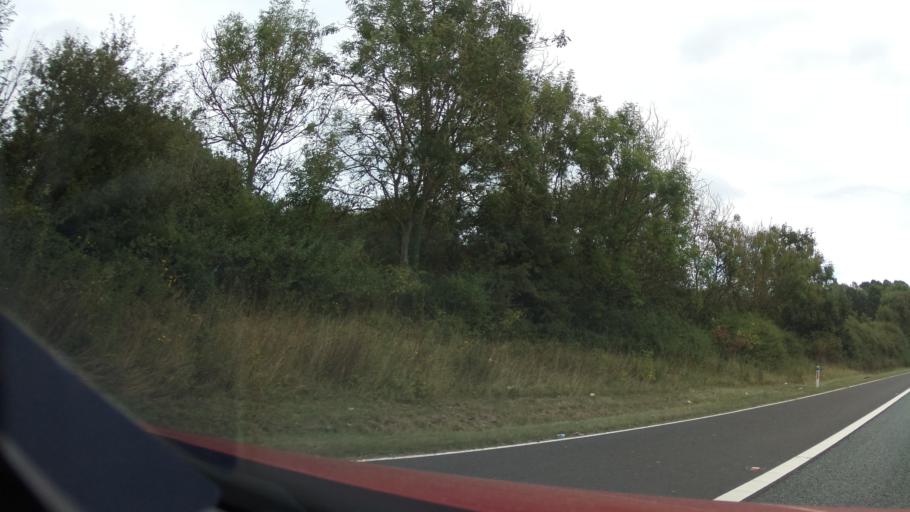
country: GB
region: England
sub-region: County Durham
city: Chester-le-Street
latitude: 54.8497
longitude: -1.5318
